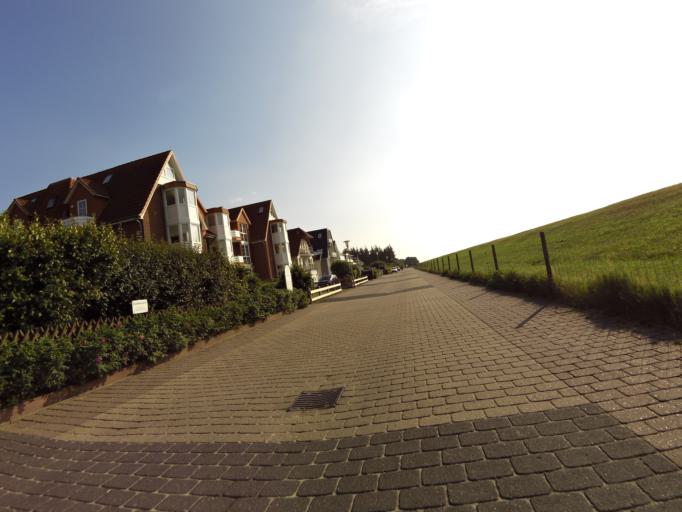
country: DE
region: Lower Saxony
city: Cuxhaven
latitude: 53.8802
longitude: 8.6246
